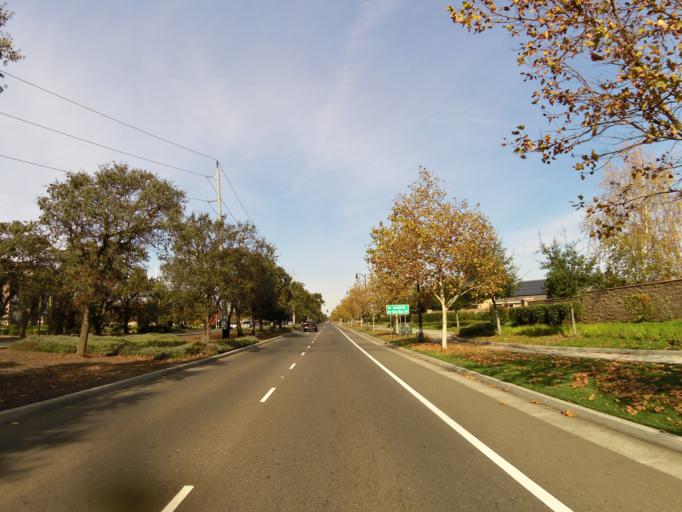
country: US
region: California
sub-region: Sacramento County
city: Laguna
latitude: 38.3956
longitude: -121.4176
